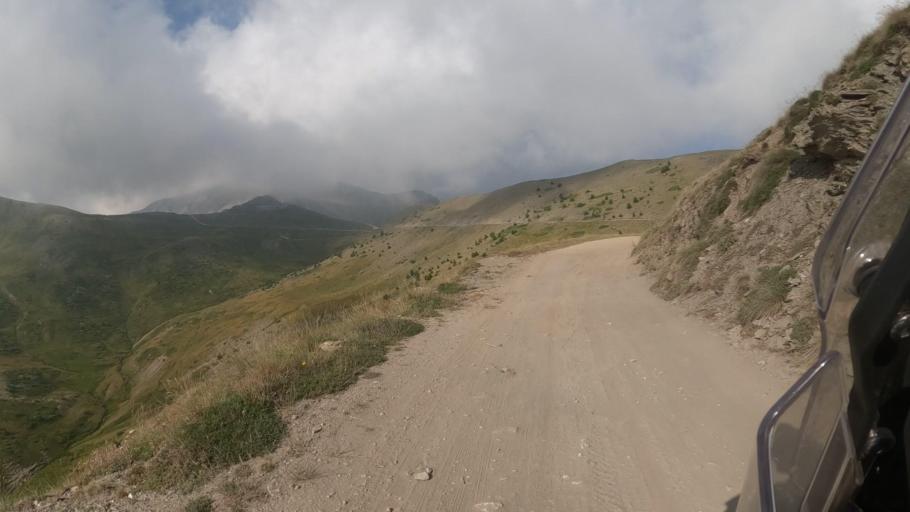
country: IT
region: Piedmont
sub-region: Provincia di Torino
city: Sestriere
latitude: 44.9919
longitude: 6.8745
